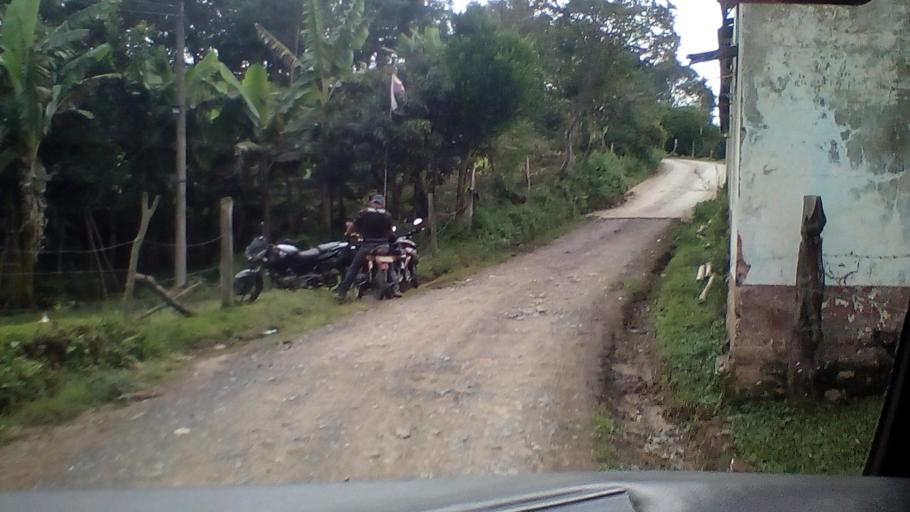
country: CO
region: Boyaca
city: Santana
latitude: 6.0074
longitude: -73.5080
